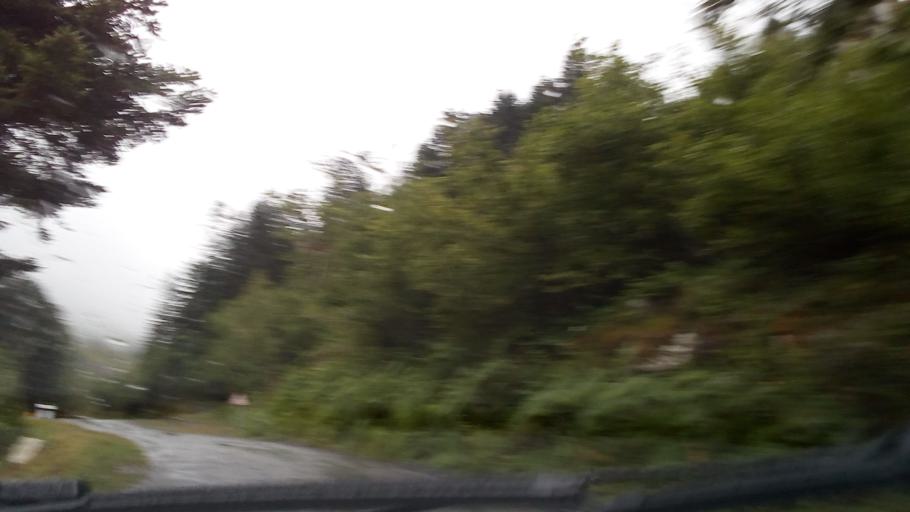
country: FR
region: Midi-Pyrenees
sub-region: Departement des Hautes-Pyrenees
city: Cauterets
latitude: 42.9077
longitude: -0.2581
